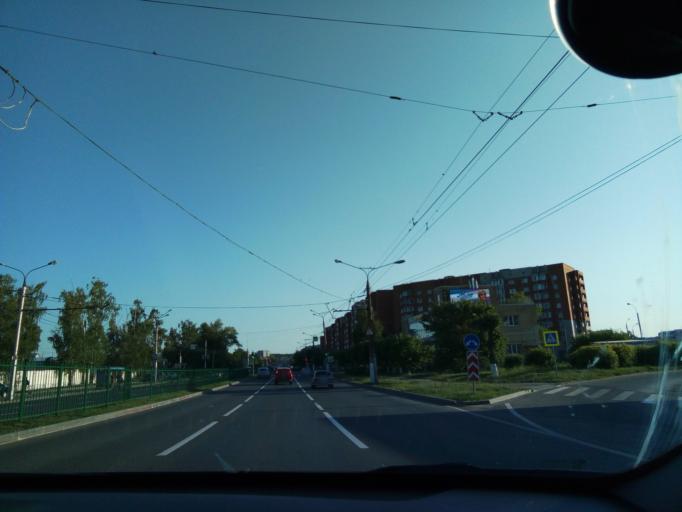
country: RU
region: Chuvashia
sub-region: Cheboksarskiy Rayon
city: Cheboksary
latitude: 56.1166
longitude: 47.2743
